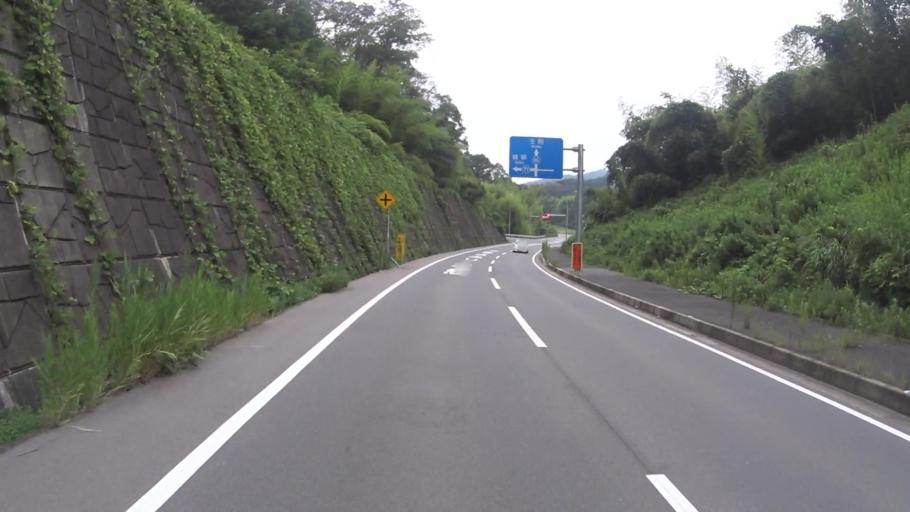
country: JP
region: Kyoto
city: Tanabe
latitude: 34.7807
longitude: 135.7556
